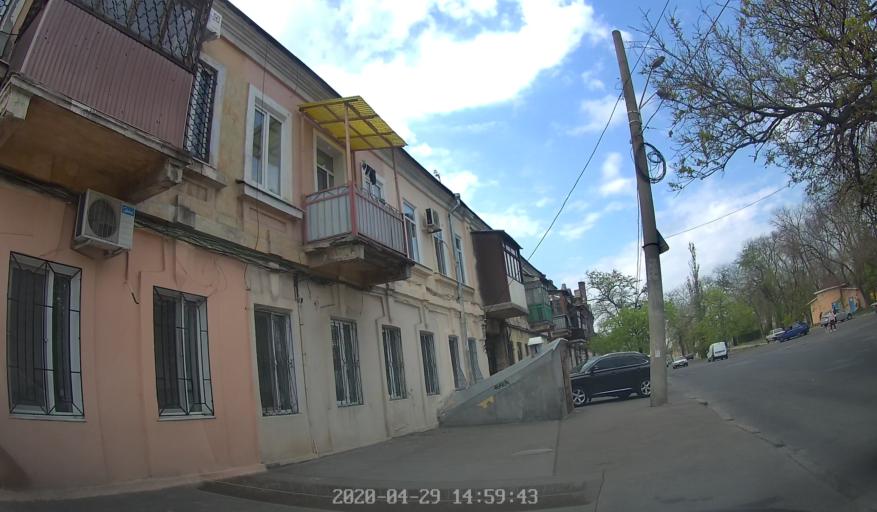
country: GR
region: South Aegean
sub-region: Nomos Kykladon
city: Serifos
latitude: 37.1909
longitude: 24.5739
